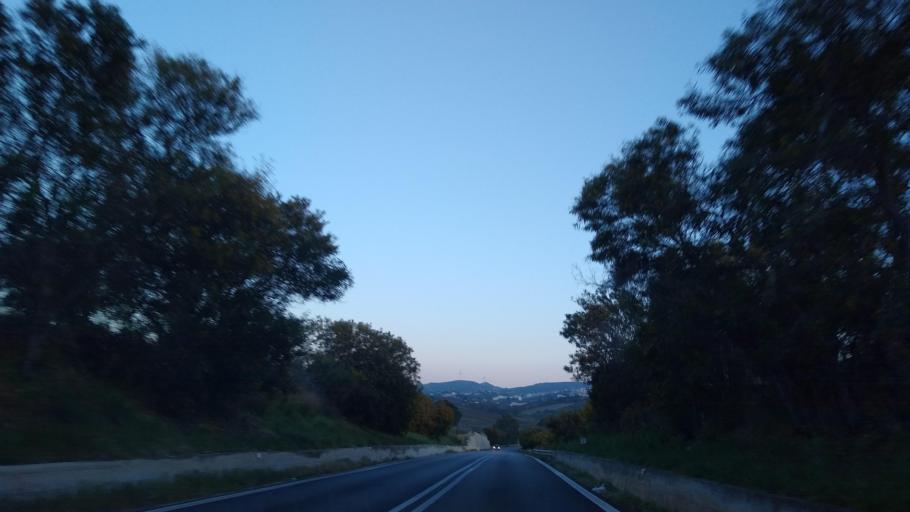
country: IT
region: Sicily
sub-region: Trapani
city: Alcamo
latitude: 38.0123
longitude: 12.9609
